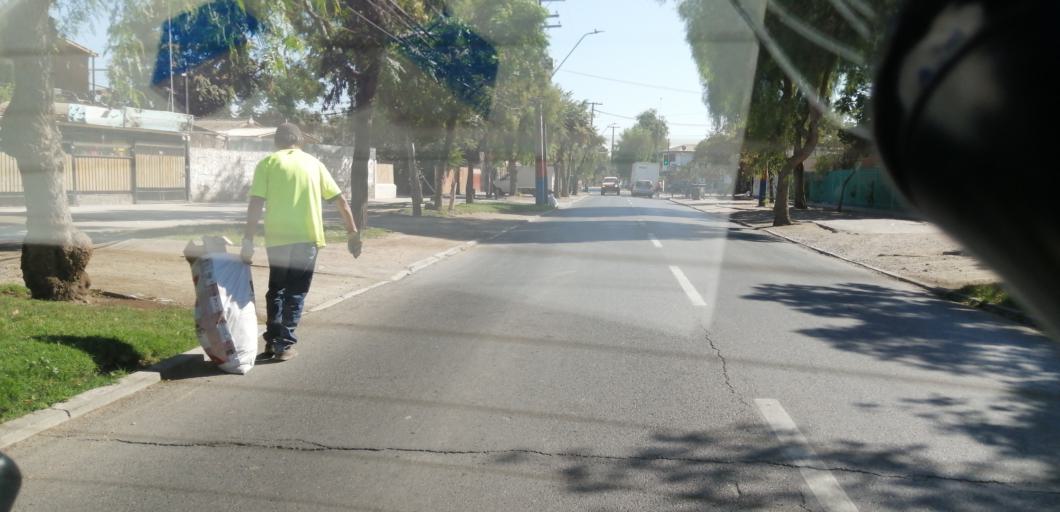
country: CL
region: Santiago Metropolitan
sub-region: Provincia de Santiago
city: Lo Prado
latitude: -33.4321
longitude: -70.7583
